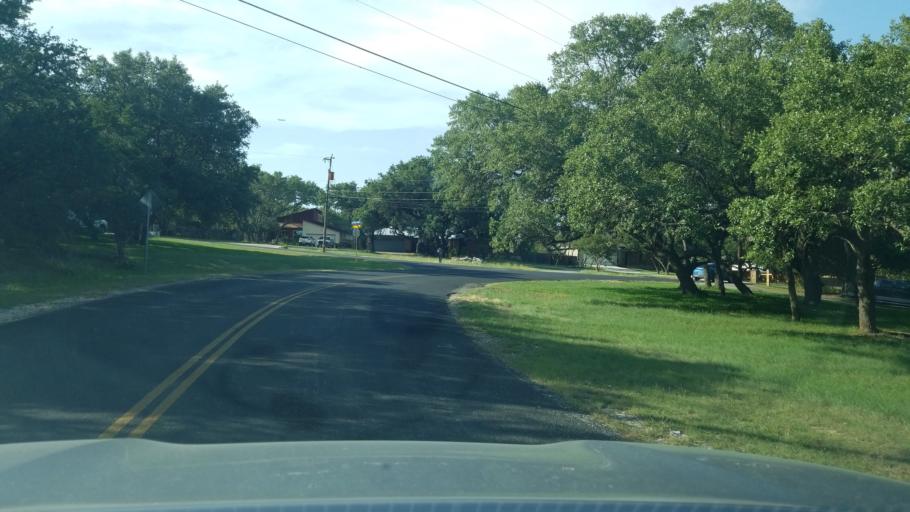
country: US
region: Texas
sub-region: Bexar County
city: Timberwood Park
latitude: 29.6871
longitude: -98.4819
